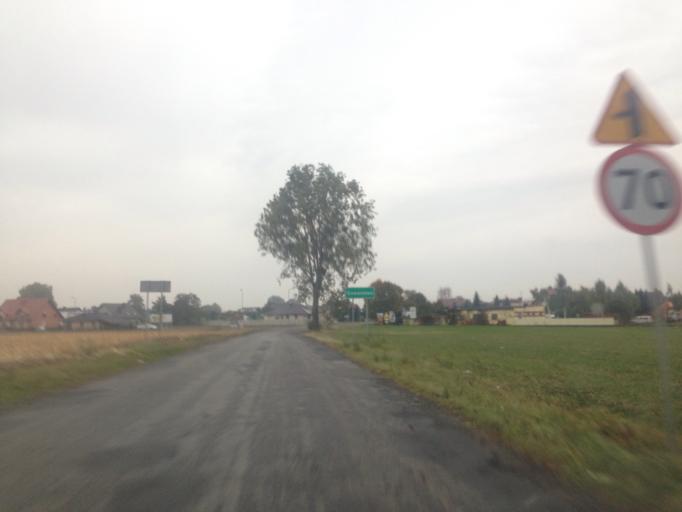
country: PL
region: Greater Poland Voivodeship
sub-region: Powiat poznanski
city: Kleszczewo
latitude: 52.3591
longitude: 17.1344
